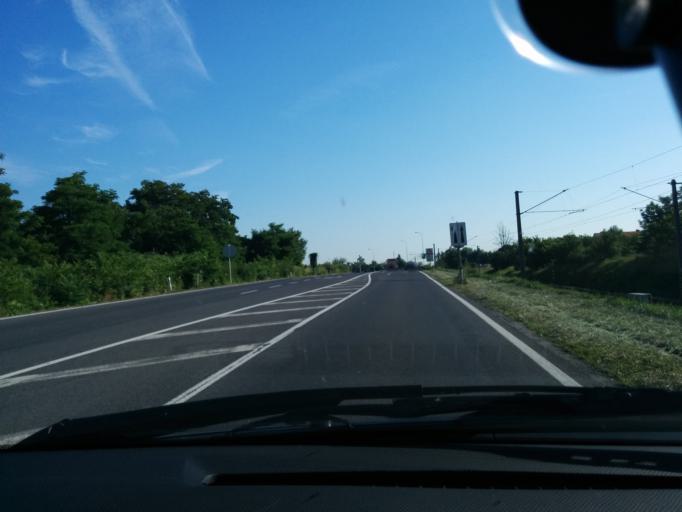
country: AT
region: Lower Austria
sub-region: Politischer Bezirk Modling
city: Neu-Guntramsdorf
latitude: 48.0619
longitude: 16.3127
